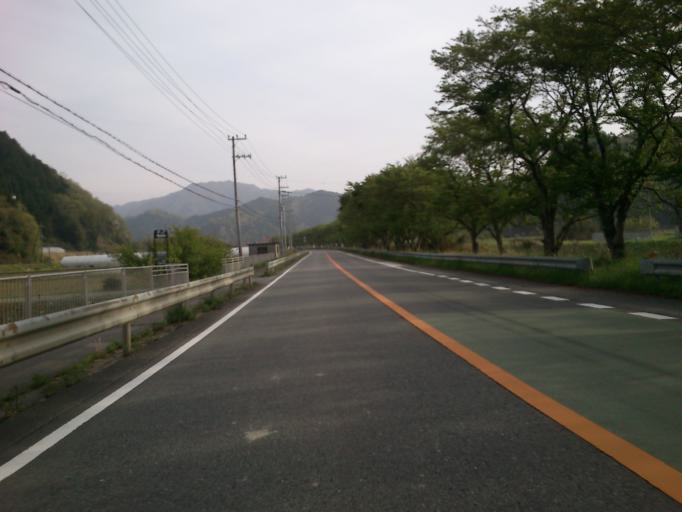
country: JP
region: Hyogo
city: Sasayama
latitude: 35.0985
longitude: 135.3161
